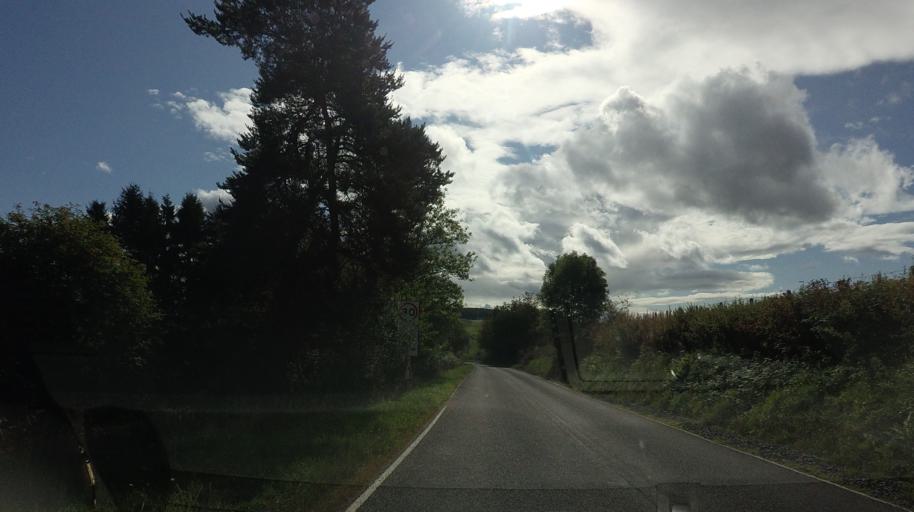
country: GB
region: Scotland
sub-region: Aberdeenshire
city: Torphins
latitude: 57.1327
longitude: -2.6944
